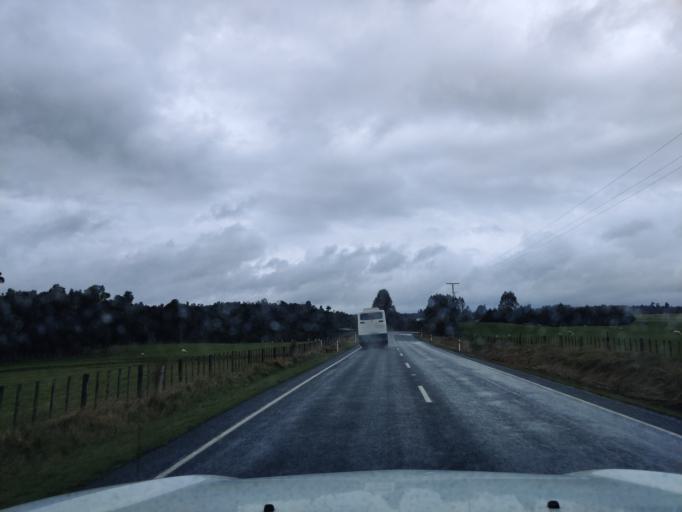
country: NZ
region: Manawatu-Wanganui
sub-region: Ruapehu District
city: Waiouru
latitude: -39.3518
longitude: 175.3599
